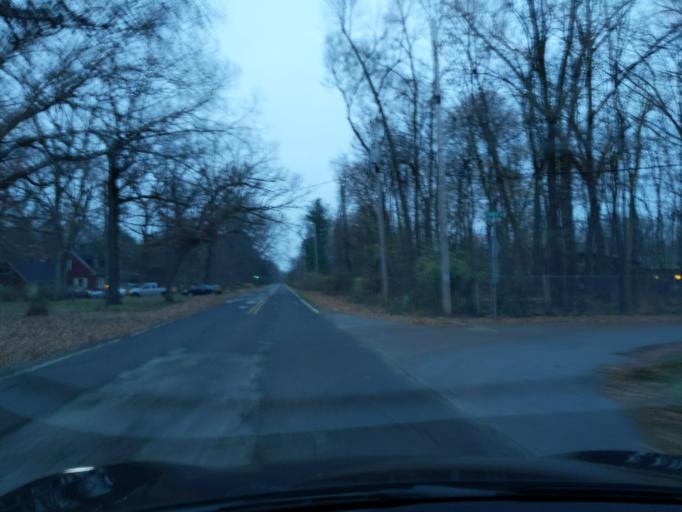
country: US
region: Indiana
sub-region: Saint Joseph County
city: Georgetown
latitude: 41.7289
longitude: -86.2555
